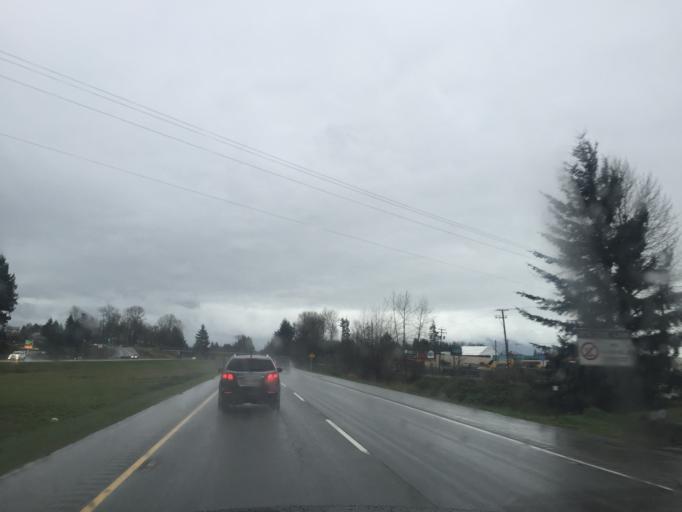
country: US
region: Washington
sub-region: Whatcom County
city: Sumas
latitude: 49.0487
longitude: -122.3606
